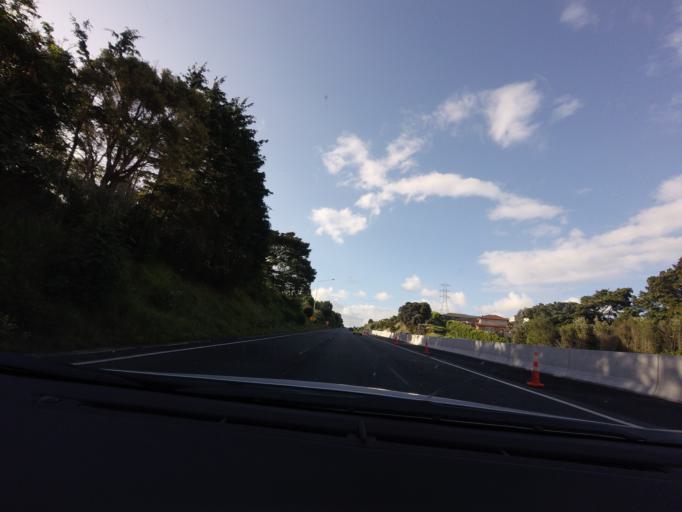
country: NZ
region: Auckland
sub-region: Auckland
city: Takanini
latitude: -37.0191
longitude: 174.9089
